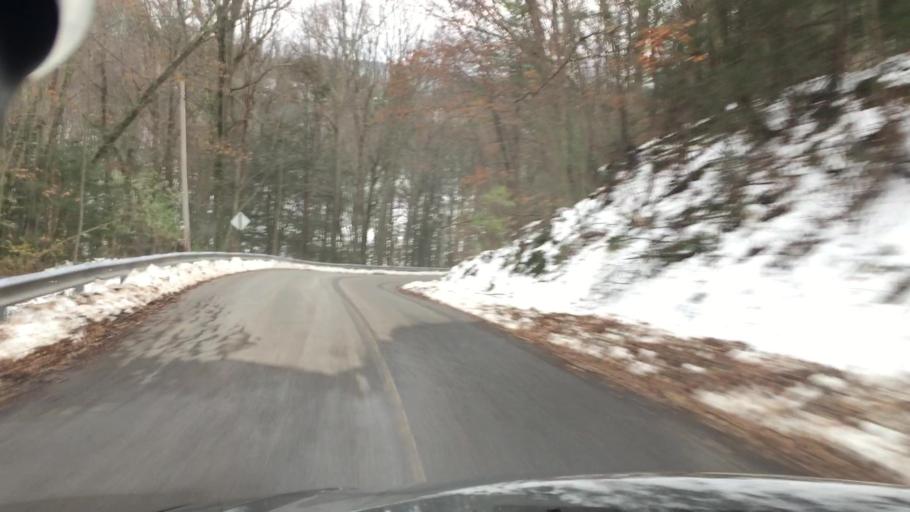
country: US
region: Pennsylvania
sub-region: Luzerne County
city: Conyngham
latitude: 41.0086
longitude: -76.1293
